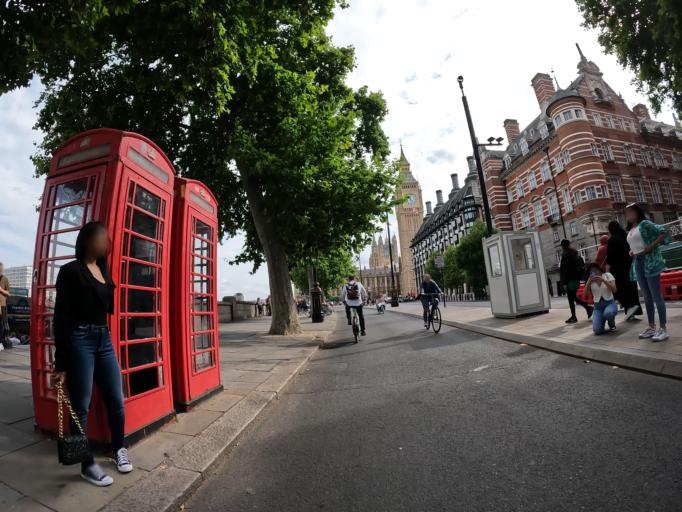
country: GB
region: England
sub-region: Greater London
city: Orpington
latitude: 51.3673
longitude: 0.0508
